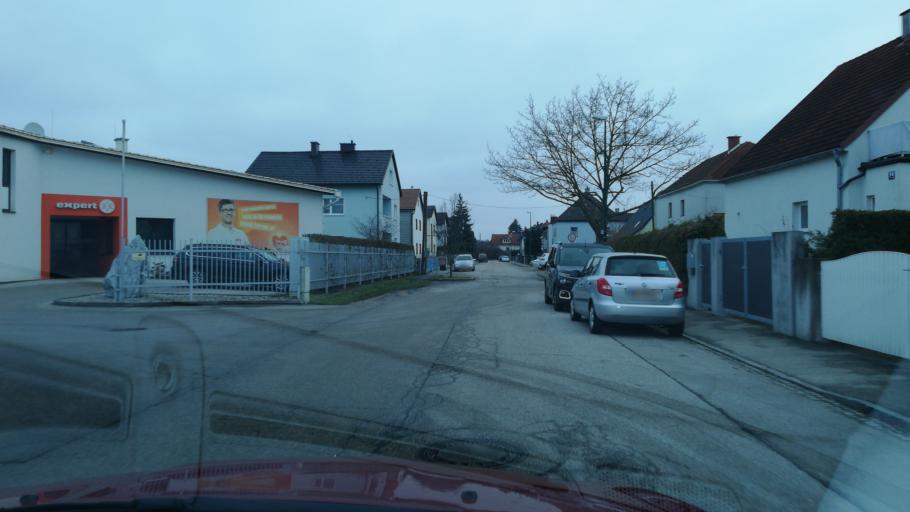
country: AT
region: Upper Austria
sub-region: Wels Stadt
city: Wels
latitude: 48.1753
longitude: 14.0519
